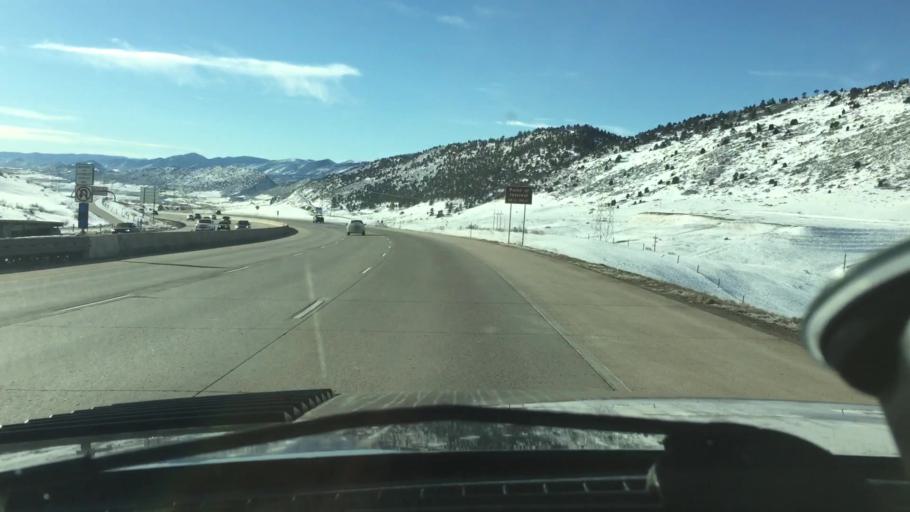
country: US
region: Colorado
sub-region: Jefferson County
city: West Pleasant View
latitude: 39.7024
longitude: -105.1937
